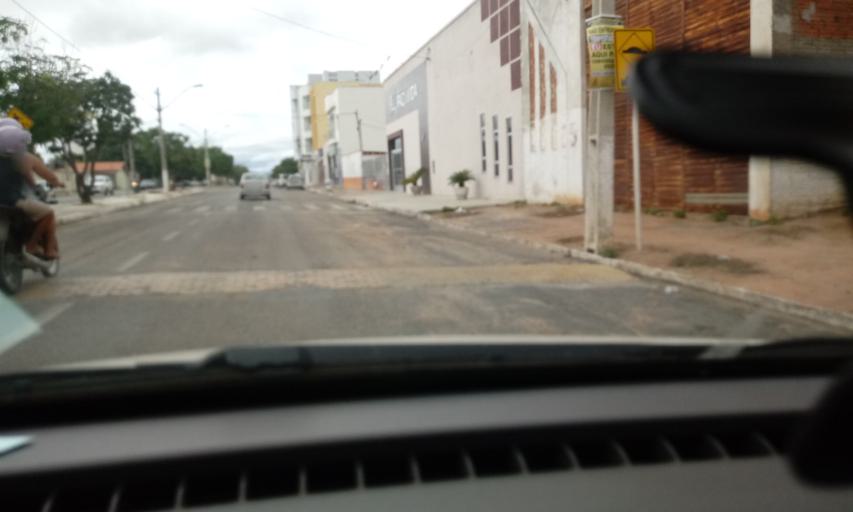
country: BR
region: Bahia
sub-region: Guanambi
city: Guanambi
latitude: -14.2148
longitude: -42.7863
